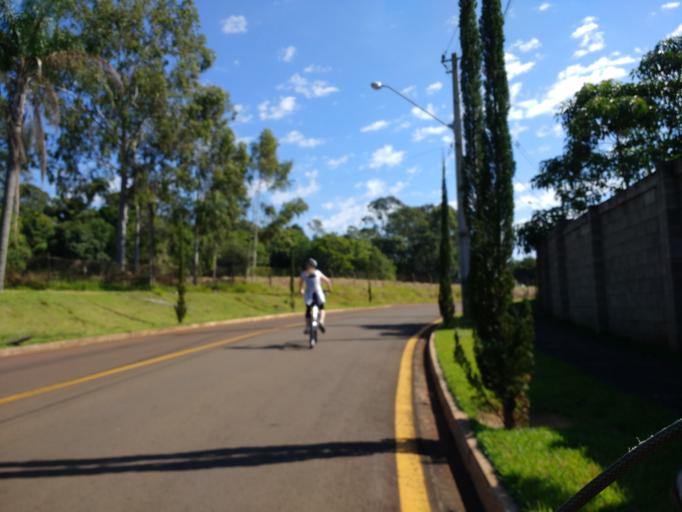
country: BR
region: Parana
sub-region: Londrina
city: Londrina
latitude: -23.3664
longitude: -51.1952
